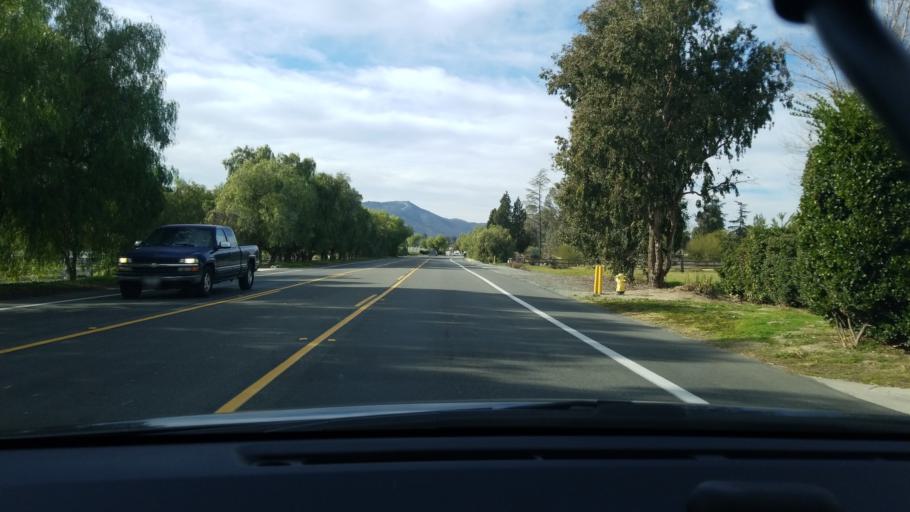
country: US
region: California
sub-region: Riverside County
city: Temecula
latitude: 33.4795
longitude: -117.1282
